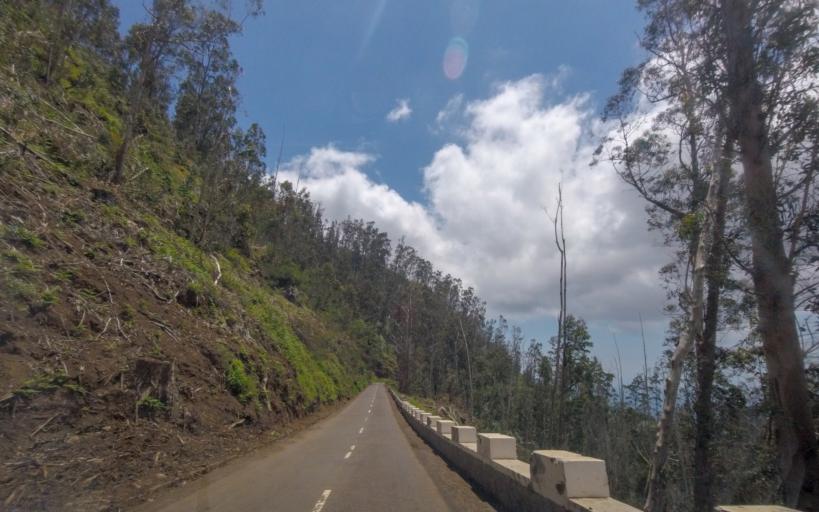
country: PT
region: Madeira
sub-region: Funchal
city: Nossa Senhora do Monte
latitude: 32.6889
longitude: -16.8896
